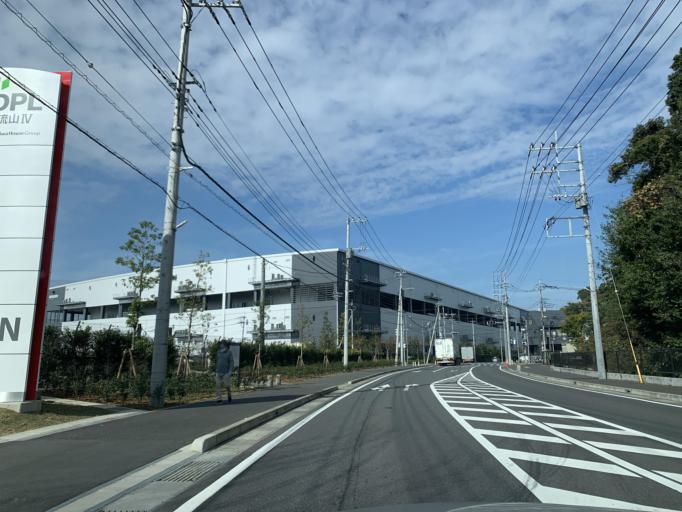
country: JP
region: Chiba
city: Nagareyama
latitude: 35.9046
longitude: 139.8935
